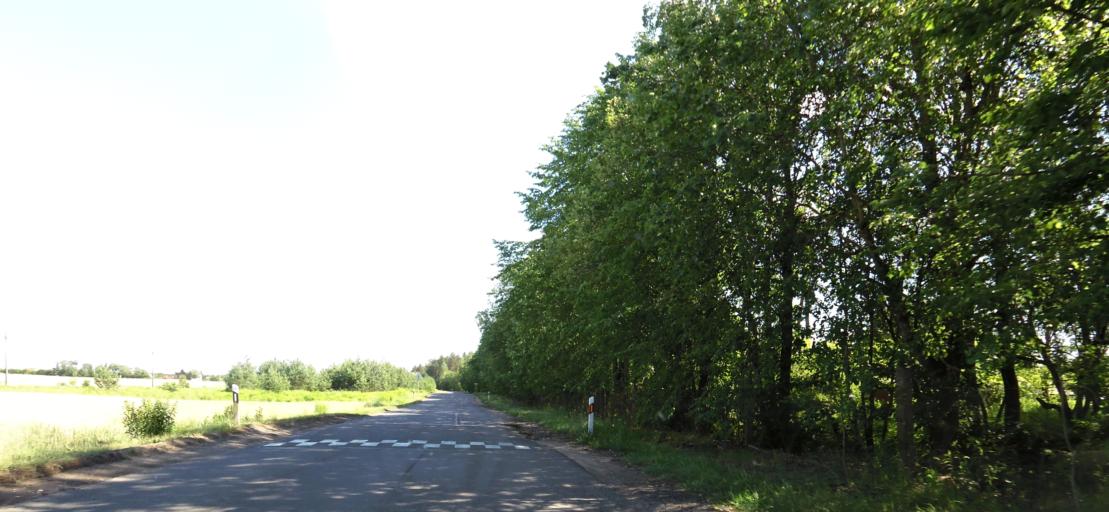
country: LT
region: Vilnius County
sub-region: Vilnius
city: Fabijoniskes
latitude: 54.8055
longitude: 25.3279
